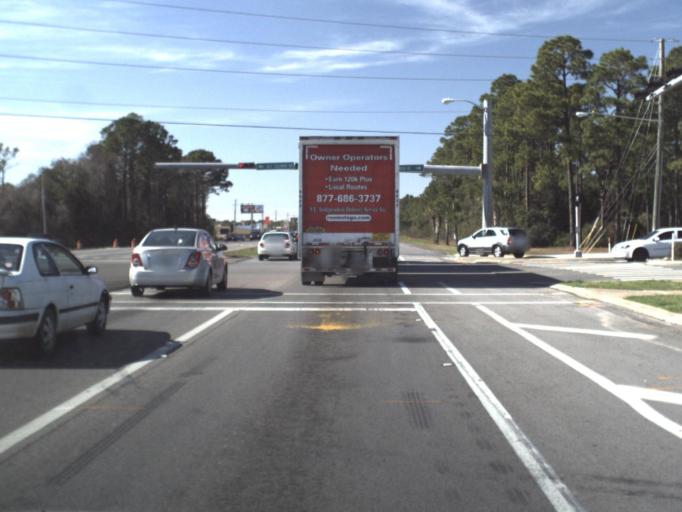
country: US
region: Florida
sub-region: Bay County
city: Panama City Beach
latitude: 30.2007
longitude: -85.8195
